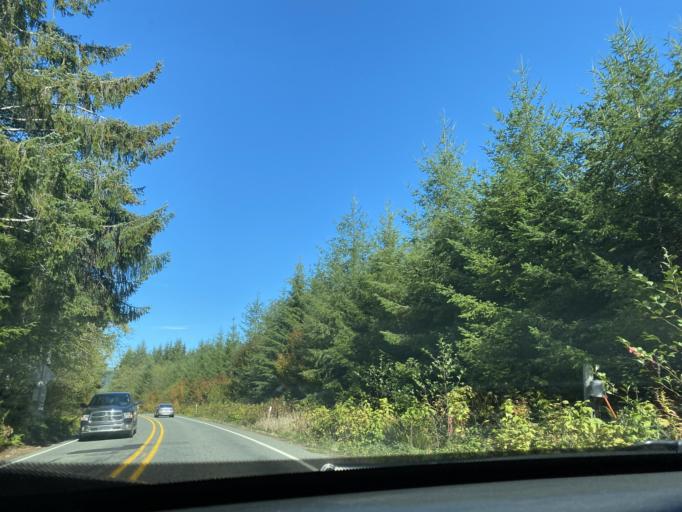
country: US
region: Washington
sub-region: Clallam County
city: Forks
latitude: 47.9452
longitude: -124.4626
